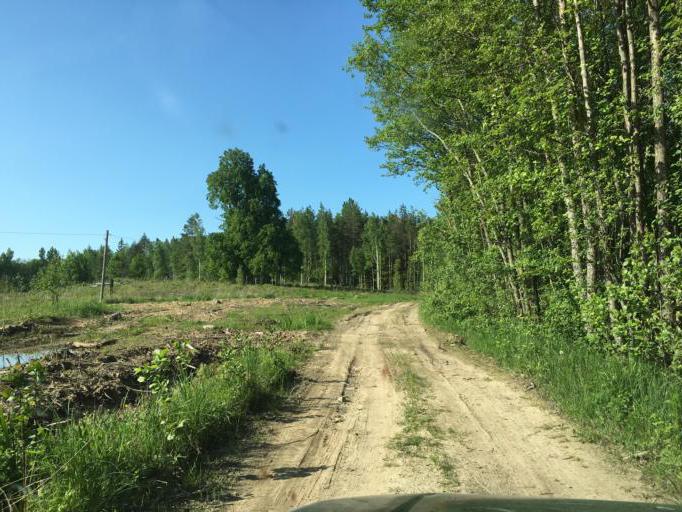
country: LV
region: Dundaga
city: Dundaga
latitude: 57.6018
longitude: 22.5077
